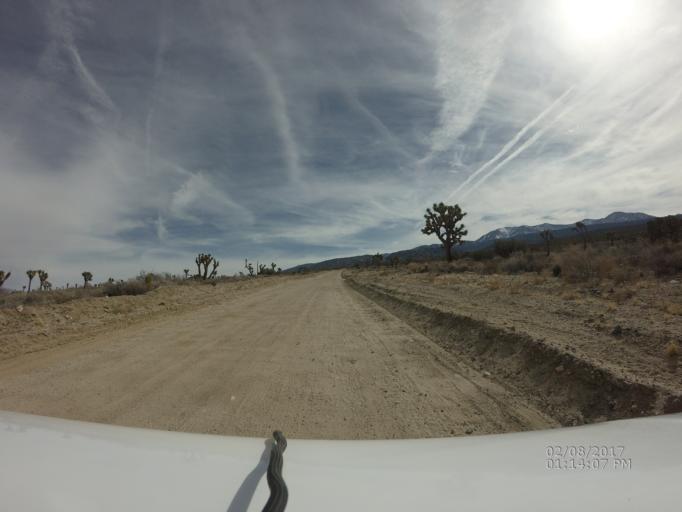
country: US
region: California
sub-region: San Bernardino County
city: Pinon Hills
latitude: 34.4743
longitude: -117.7789
